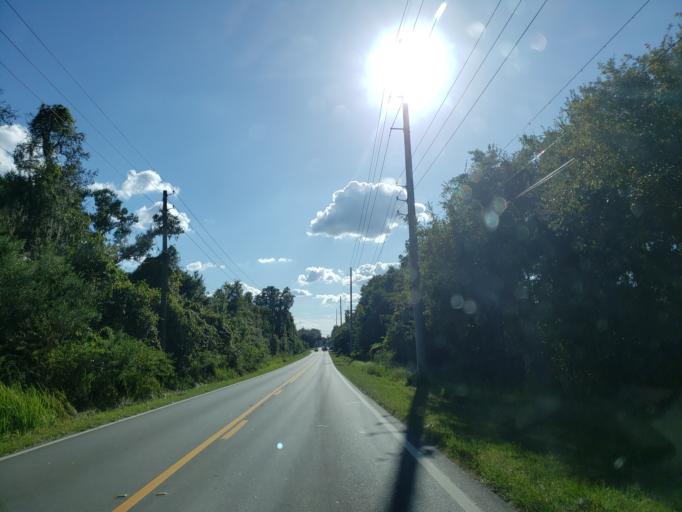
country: US
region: Florida
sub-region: Hillsborough County
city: Dover
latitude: 27.9877
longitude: -82.1678
